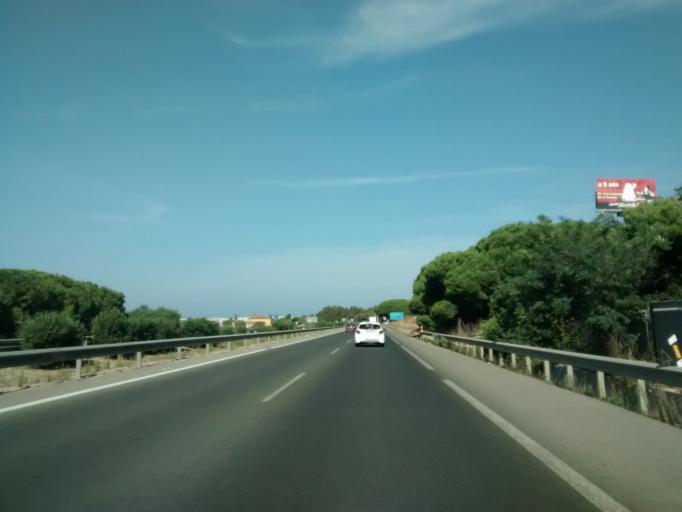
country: ES
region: Andalusia
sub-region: Provincia de Cadiz
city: Chiclana de la Frontera
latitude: 36.4425
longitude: -6.1332
